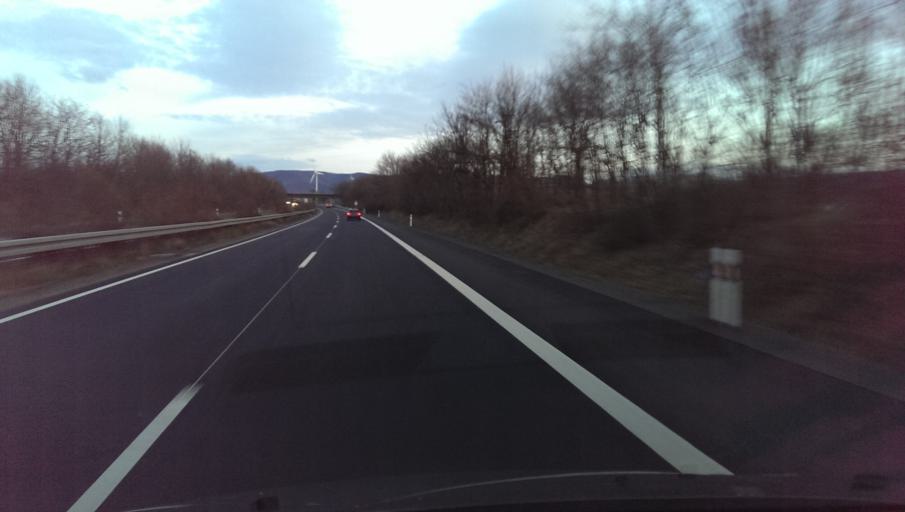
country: DE
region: Lower Saxony
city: Bad Harzburg
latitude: 51.9151
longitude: 10.5262
